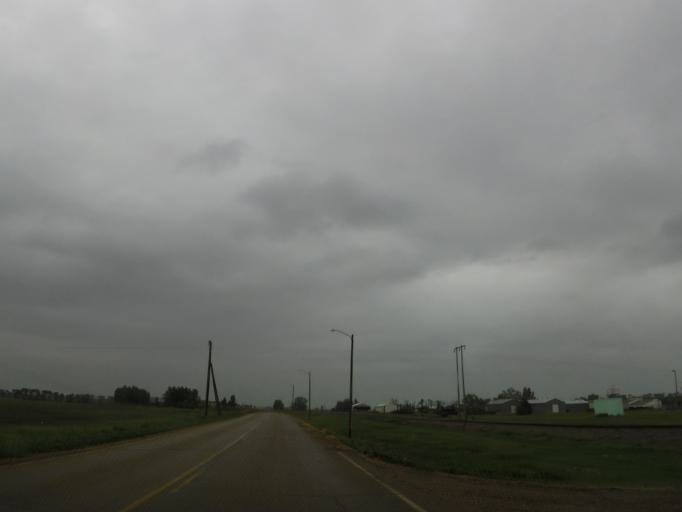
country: US
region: North Dakota
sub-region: Walsh County
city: Grafton
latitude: 48.4287
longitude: -97.4055
